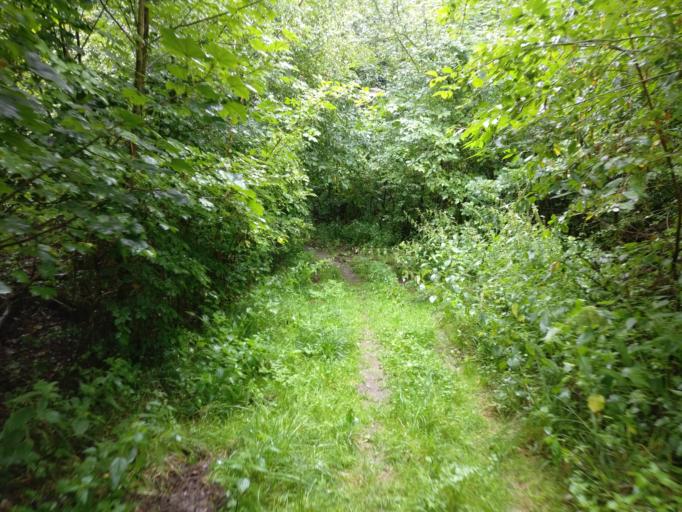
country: DE
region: Hesse
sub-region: Regierungsbezirk Giessen
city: Greifenstein
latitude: 50.6224
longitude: 8.2804
